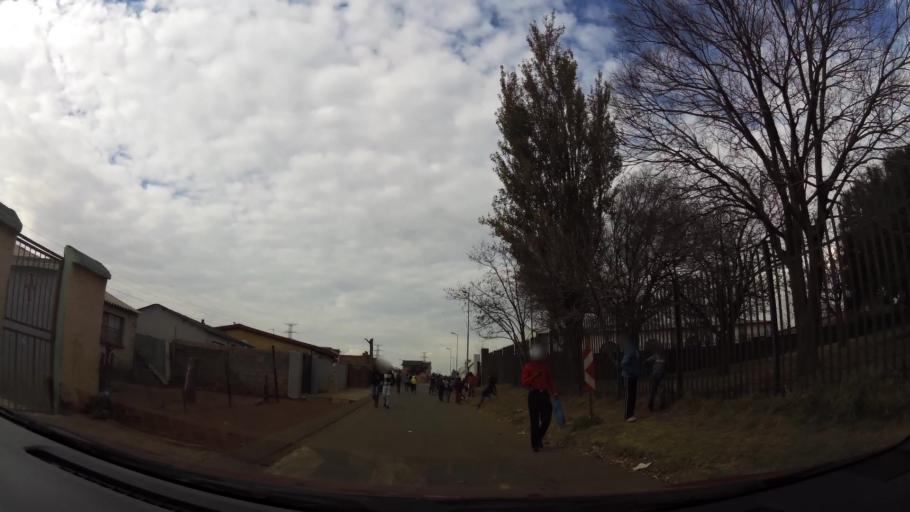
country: ZA
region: Gauteng
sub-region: City of Johannesburg Metropolitan Municipality
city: Soweto
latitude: -26.2419
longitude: 27.8517
